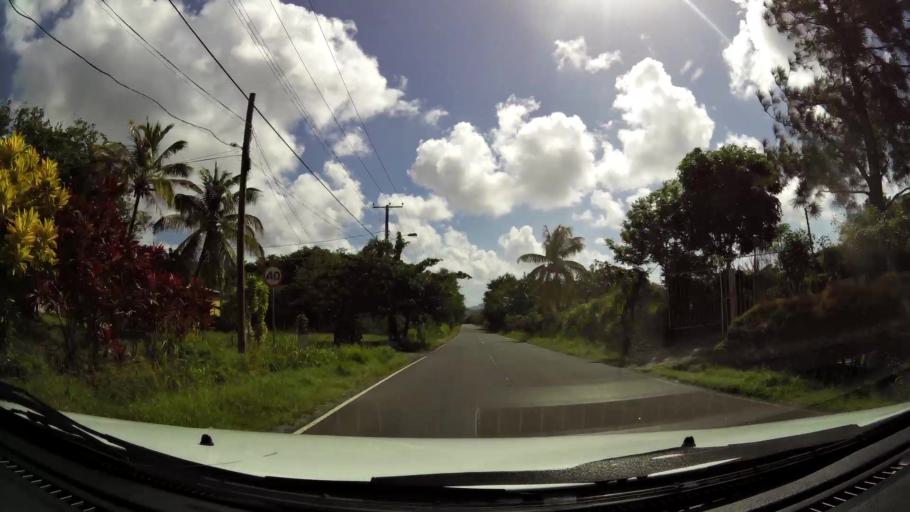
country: LC
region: Choiseul Quarter
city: Choiseul
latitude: 13.7587
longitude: -61.0186
